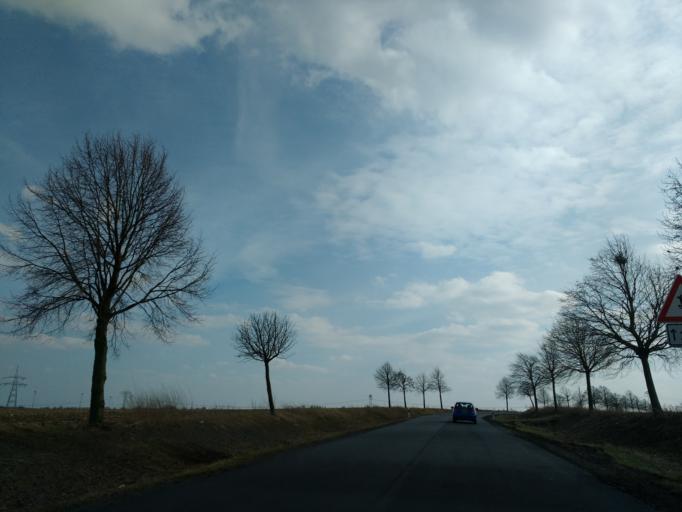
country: DE
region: Saxony-Anhalt
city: Schraplau
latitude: 51.4260
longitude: 11.6497
